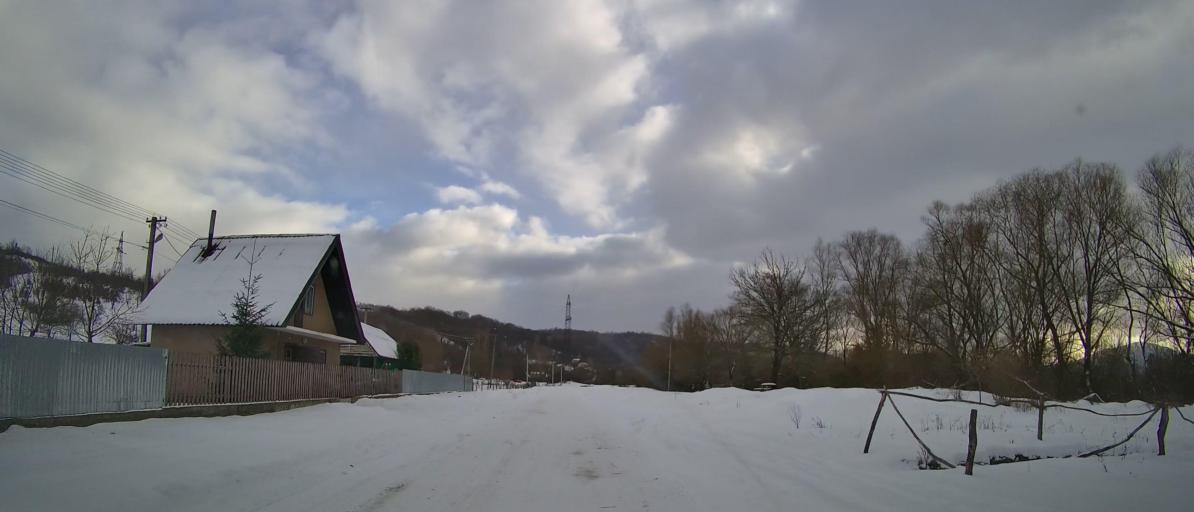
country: UA
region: Zakarpattia
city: Velykyi Bereznyi
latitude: 48.9097
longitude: 22.4668
